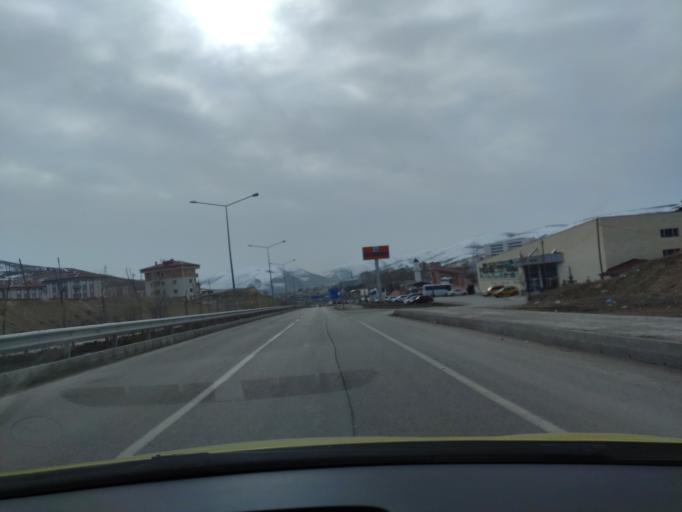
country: TR
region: Bayburt
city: Bayburt
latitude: 40.2639
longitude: 40.2060
